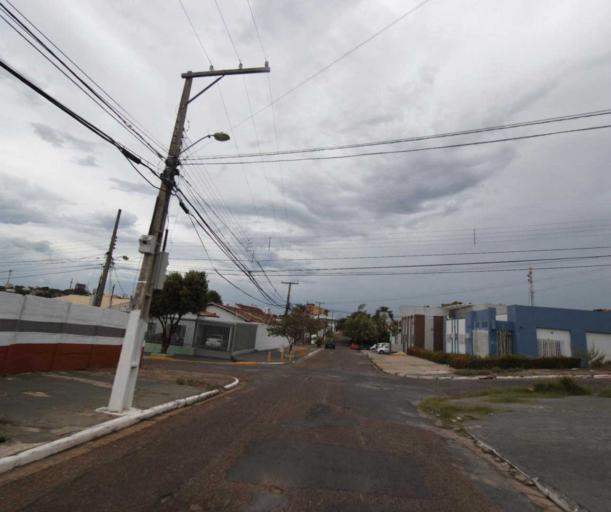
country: BR
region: Mato Grosso
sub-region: Cuiaba
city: Cuiaba
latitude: -15.6053
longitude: -56.0828
